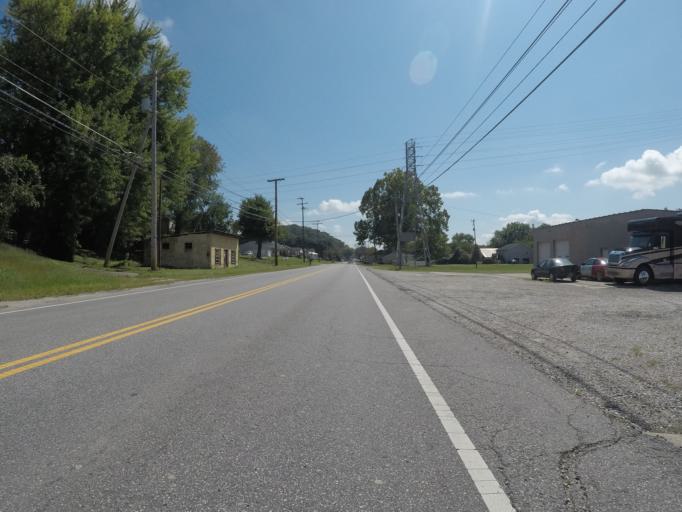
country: US
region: Ohio
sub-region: Lawrence County
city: South Point
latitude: 38.4120
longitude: -82.5787
